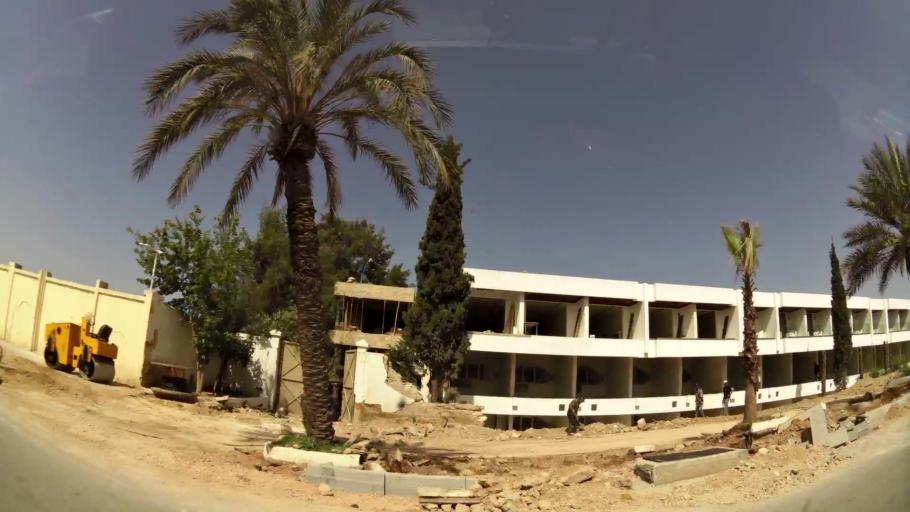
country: MA
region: Meknes-Tafilalet
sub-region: Meknes
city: Meknes
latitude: 33.8803
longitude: -5.5330
